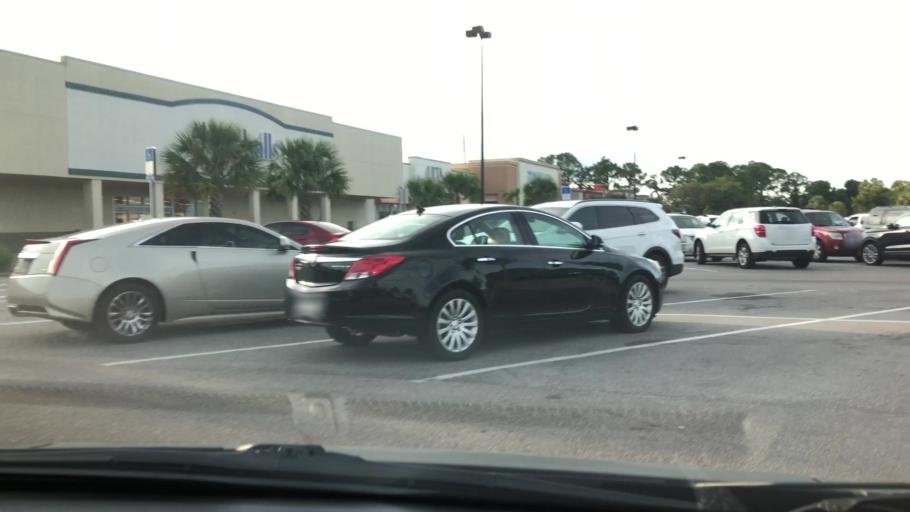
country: US
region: Florida
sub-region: Saint Johns County
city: Saint Augustine South
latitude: 29.8682
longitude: -81.3246
